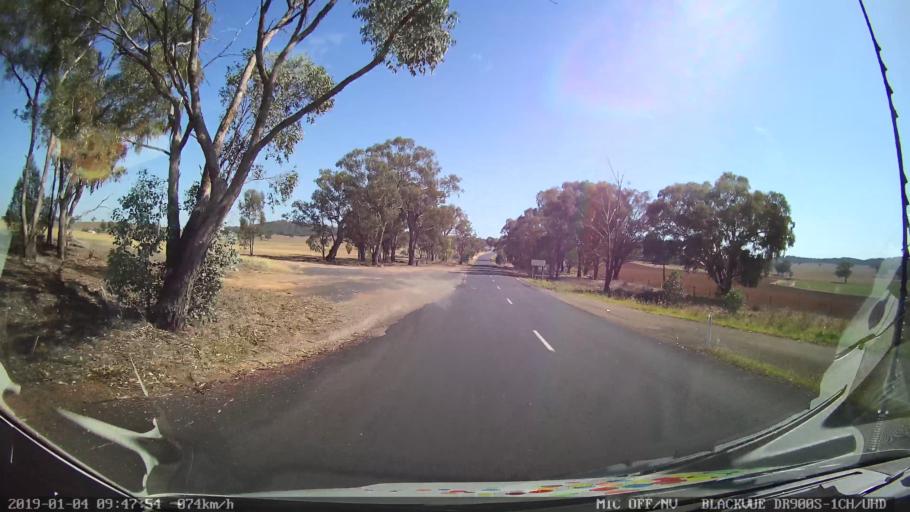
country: AU
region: New South Wales
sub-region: Cabonne
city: Canowindra
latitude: -33.6018
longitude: 148.4318
